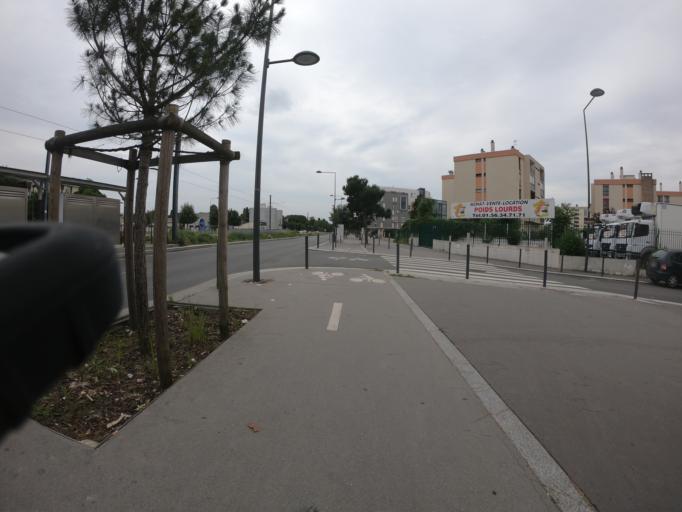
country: FR
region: Ile-de-France
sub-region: Departement du Val-de-Marne
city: Chevilly-Larue
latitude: 48.7682
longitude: 2.3679
